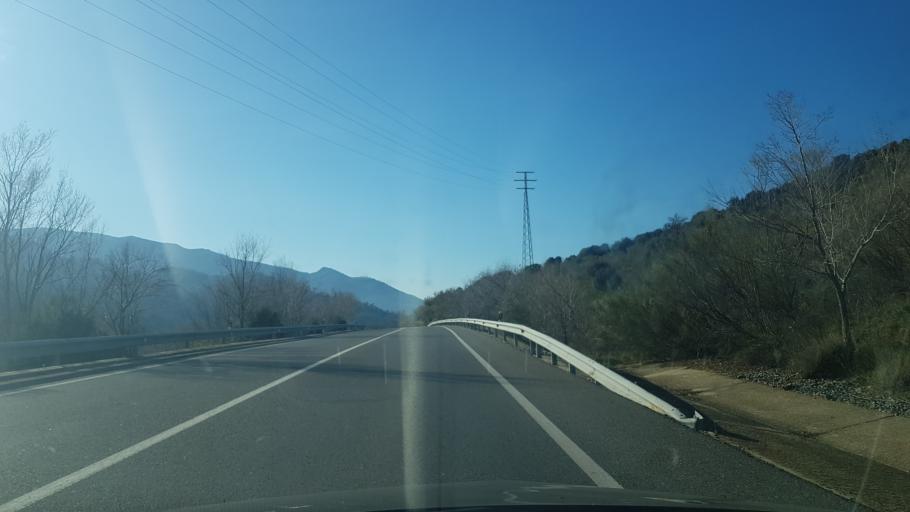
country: ES
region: Castille and Leon
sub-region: Provincia de Avila
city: El Tiemblo
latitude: 40.4278
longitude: -4.5303
